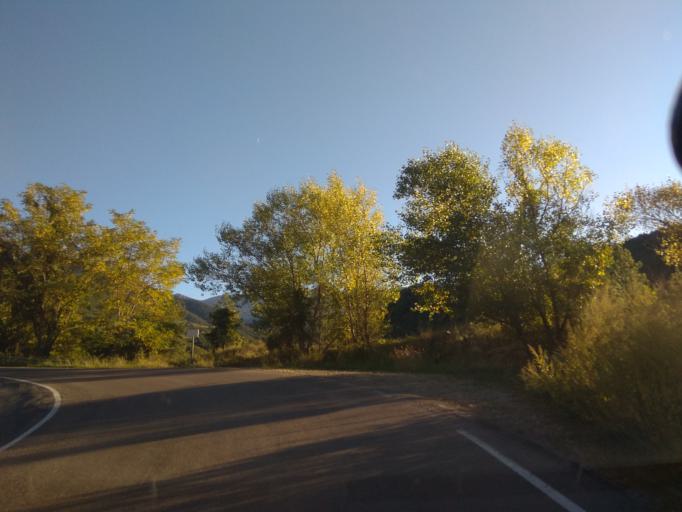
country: ES
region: Catalonia
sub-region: Provincia de Lleida
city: Lles de Cerdanya
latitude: 42.3568
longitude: 1.6869
